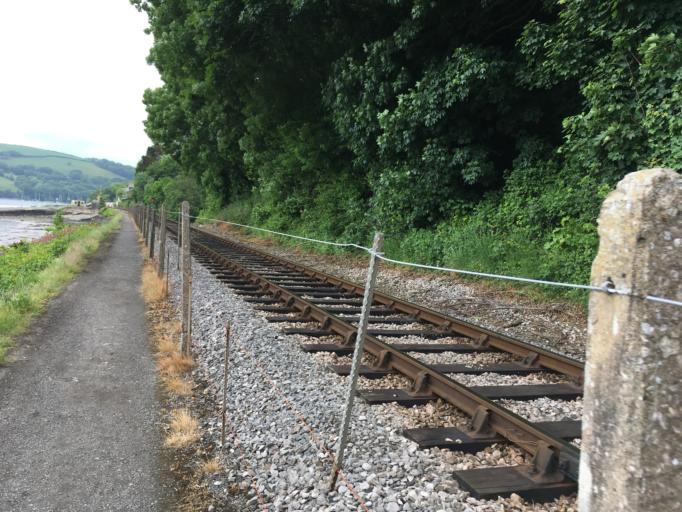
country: GB
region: England
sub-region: Devon
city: Dartmouth
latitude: 50.3582
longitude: -3.5714
